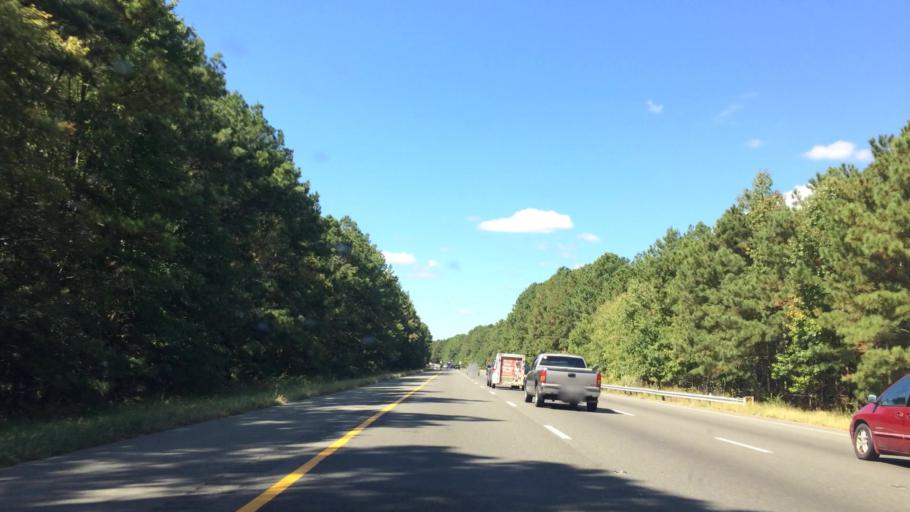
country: US
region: Virginia
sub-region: Henrico County
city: Glen Allen
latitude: 37.6713
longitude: -77.4910
